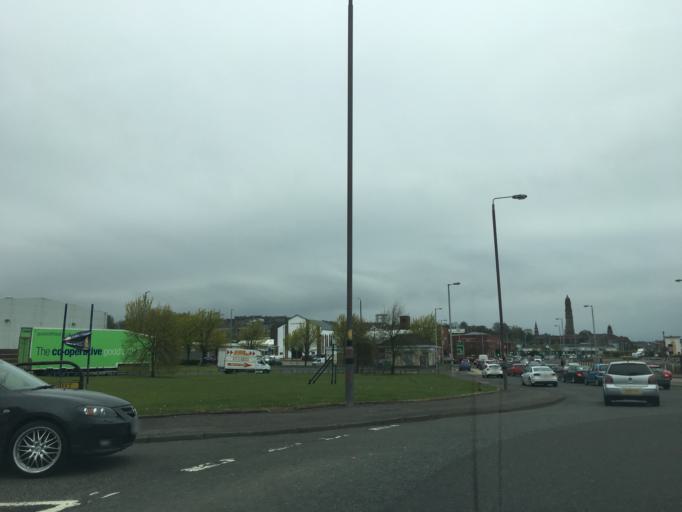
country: GB
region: Scotland
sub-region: Inverclyde
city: Greenock
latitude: 55.9436
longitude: -4.7440
